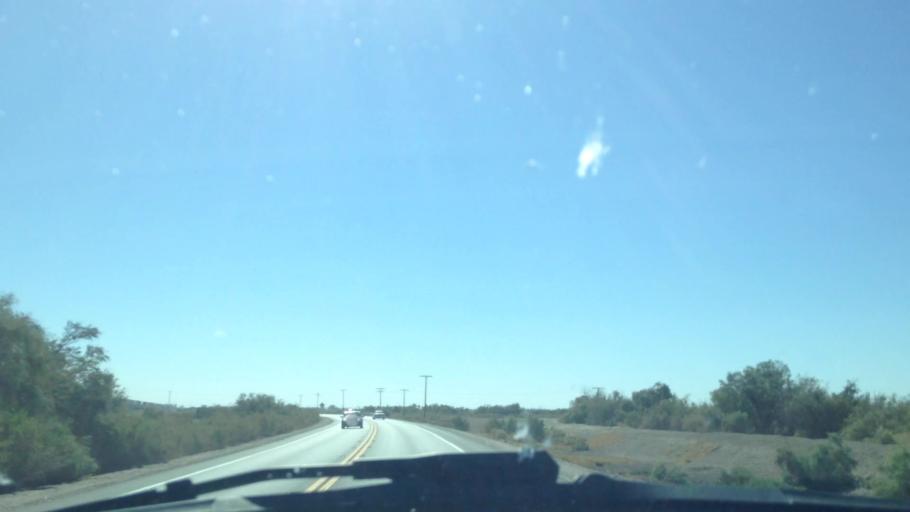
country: US
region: California
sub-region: Riverside County
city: Mecca
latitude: 33.5567
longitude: -116.0664
